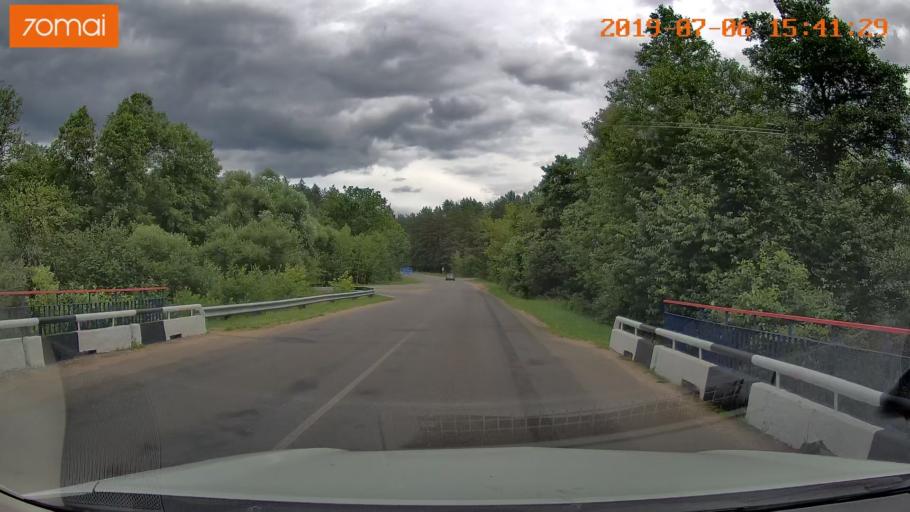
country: BY
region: Minsk
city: Rakaw
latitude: 53.9843
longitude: 26.9862
